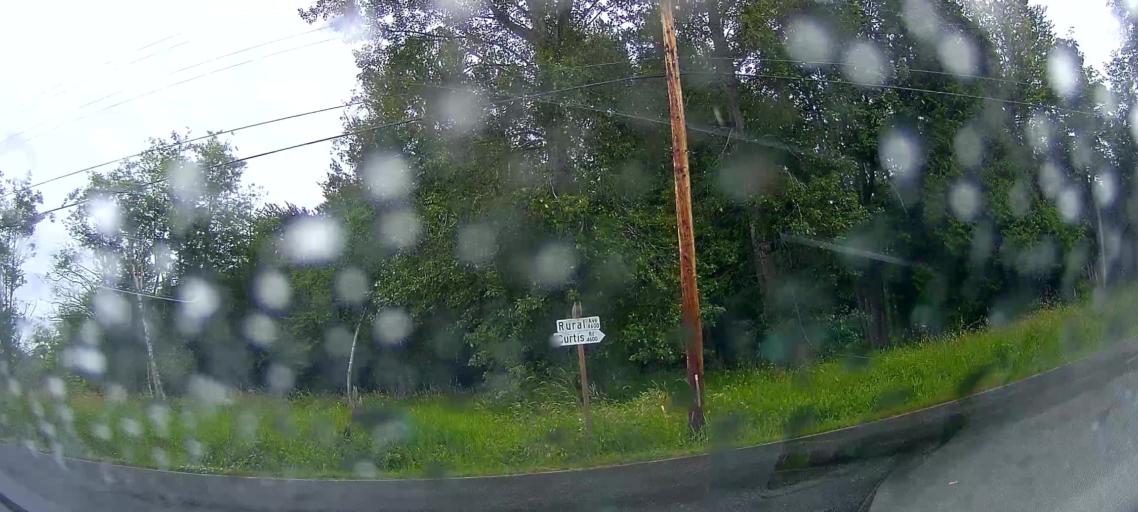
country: US
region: Washington
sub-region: Whatcom County
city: Marietta-Alderwood
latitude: 48.8112
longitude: -122.5628
